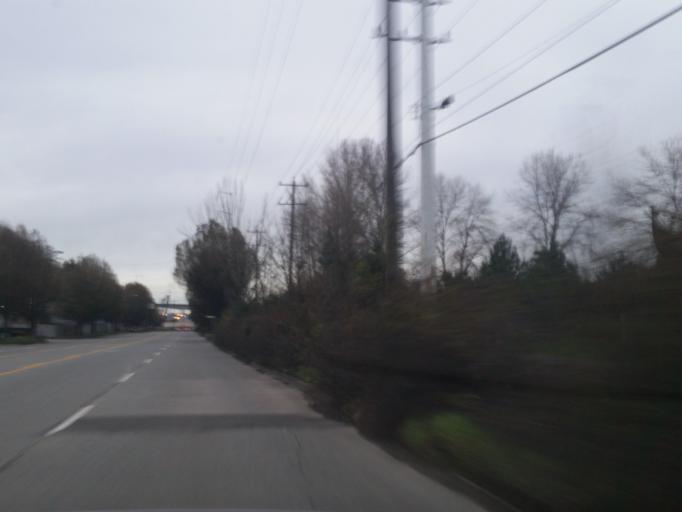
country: US
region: Washington
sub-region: King County
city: White Center
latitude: 47.5585
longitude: -122.3517
